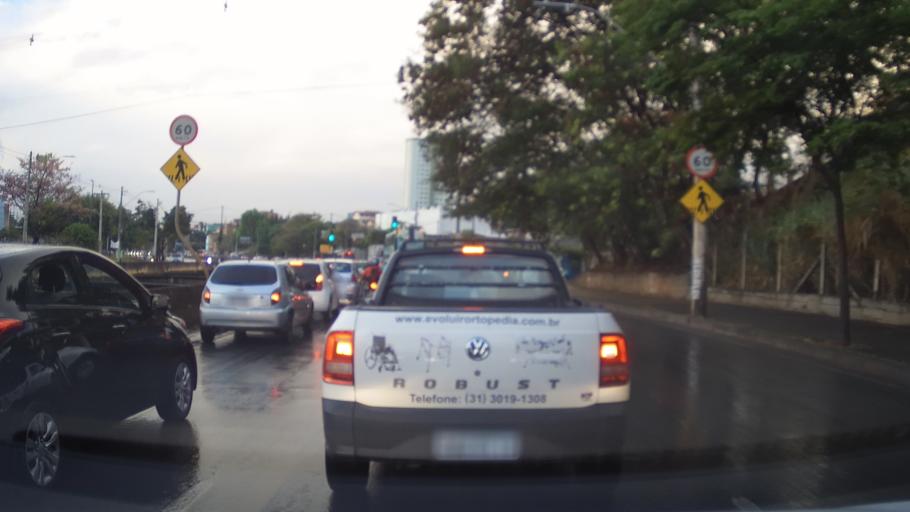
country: BR
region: Minas Gerais
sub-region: Belo Horizonte
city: Belo Horizonte
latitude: -19.9345
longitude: -43.9827
